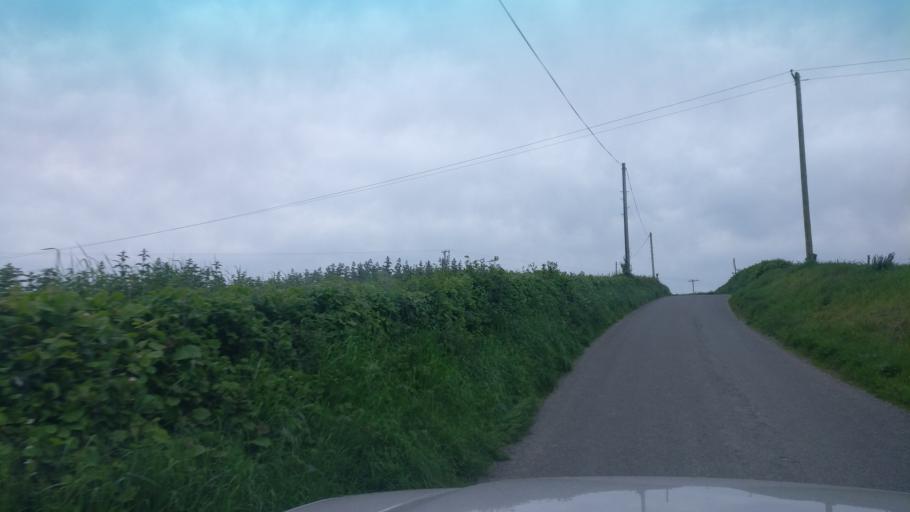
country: IE
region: Connaught
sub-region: County Galway
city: Portumna
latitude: 53.1320
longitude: -8.2910
